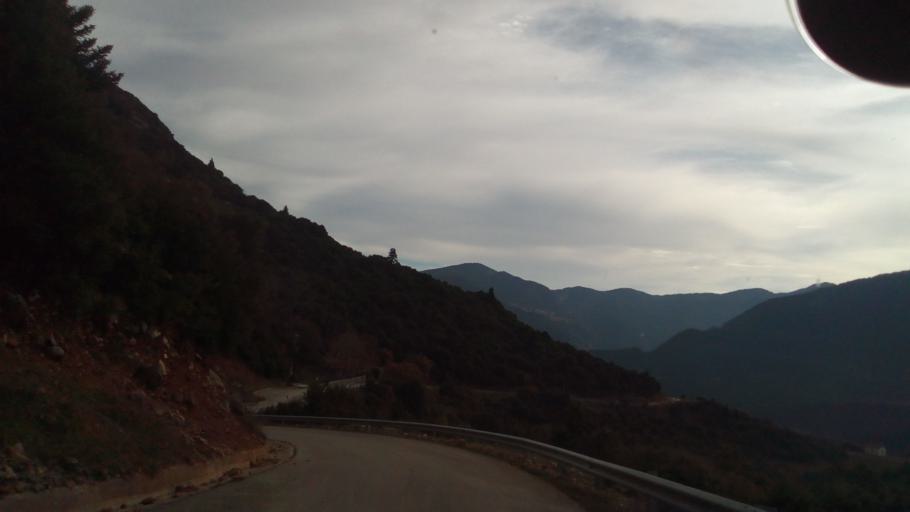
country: GR
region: West Greece
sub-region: Nomos Aitolias kai Akarnanias
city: Thermo
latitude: 38.6788
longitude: 21.8795
